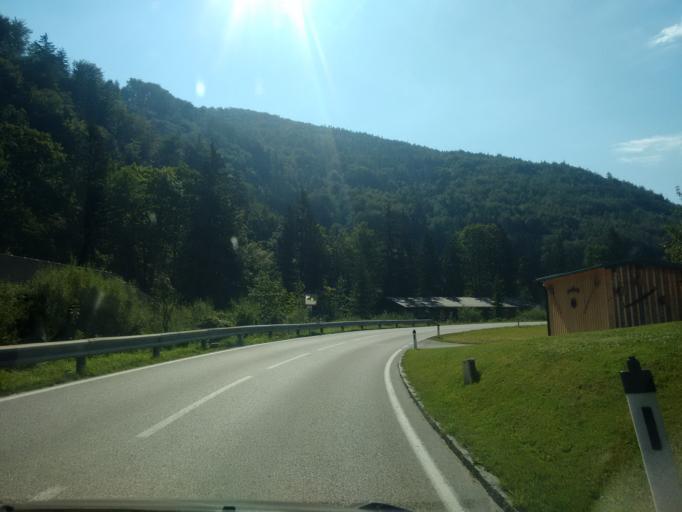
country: AT
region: Upper Austria
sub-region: Politischer Bezirk Gmunden
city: Gruenau im Almtal
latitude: 47.8454
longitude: 13.9501
